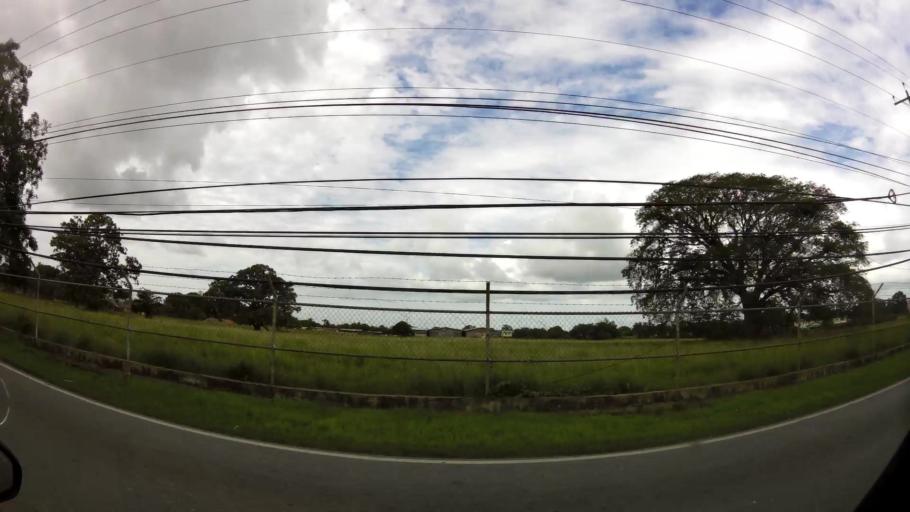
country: TT
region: Chaguanas
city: Chaguanas
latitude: 10.4681
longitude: -61.4159
